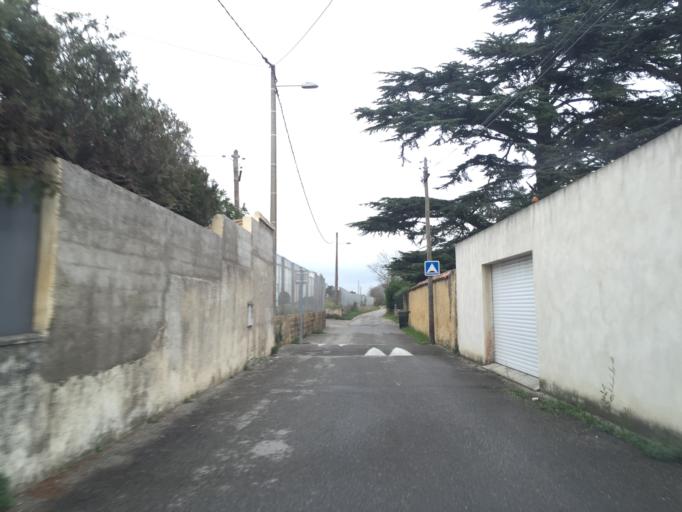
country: FR
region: Provence-Alpes-Cote d'Azur
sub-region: Departement du Vaucluse
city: Sorgues
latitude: 44.0209
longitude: 4.8730
